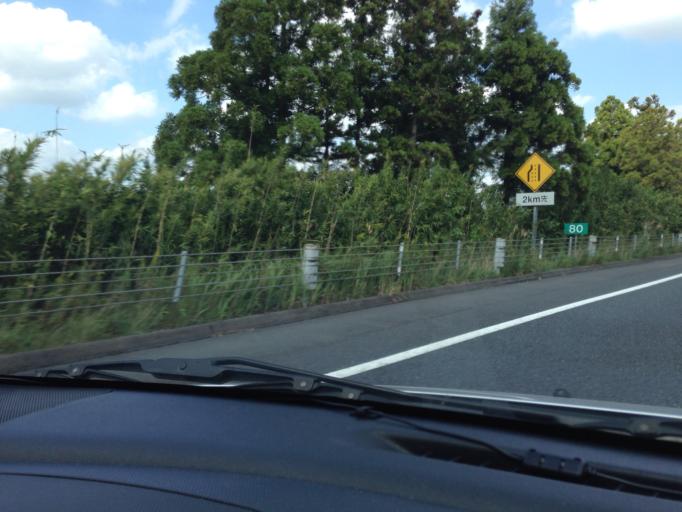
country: JP
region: Ibaraki
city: Mito-shi
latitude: 36.3654
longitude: 140.3801
